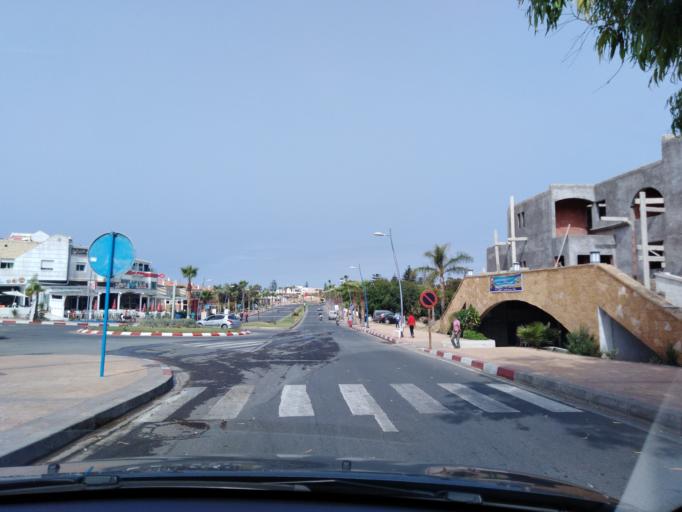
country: MA
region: Doukkala-Abda
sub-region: Safi
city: Safi
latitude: 32.7329
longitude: -9.0395
